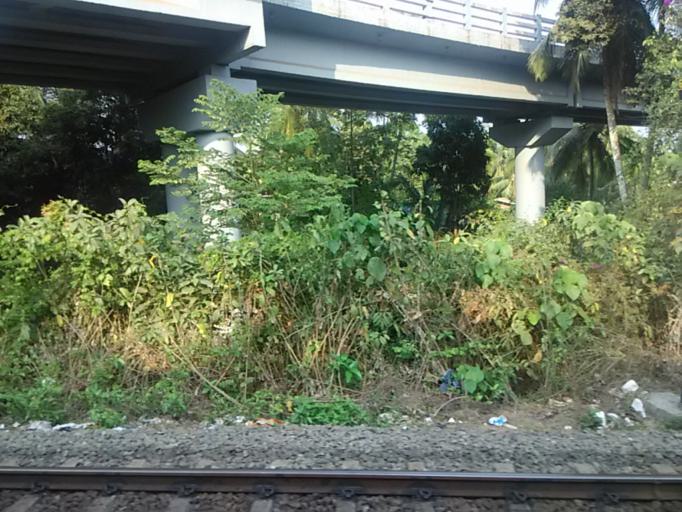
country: IN
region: Kerala
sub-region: Malappuram
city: Pariyapuram
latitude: 11.0526
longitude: 75.8577
